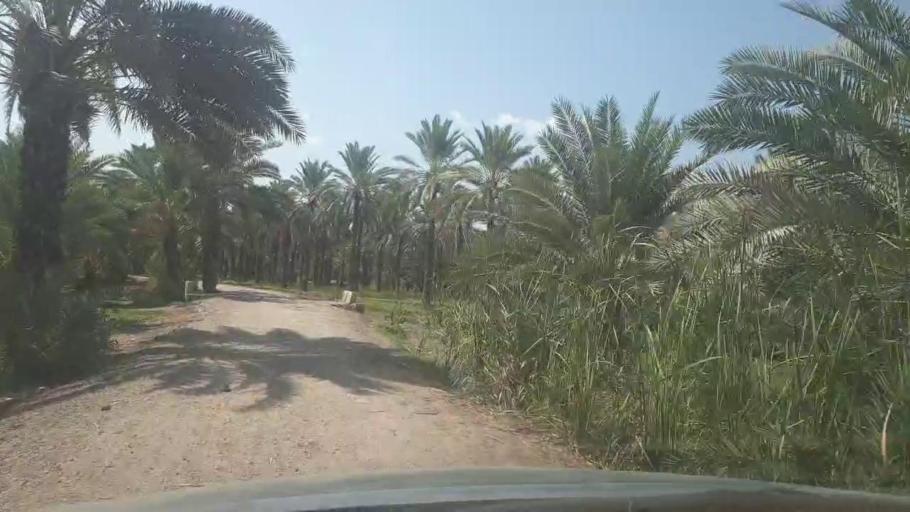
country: PK
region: Sindh
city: Khairpur
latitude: 27.5542
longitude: 68.8039
